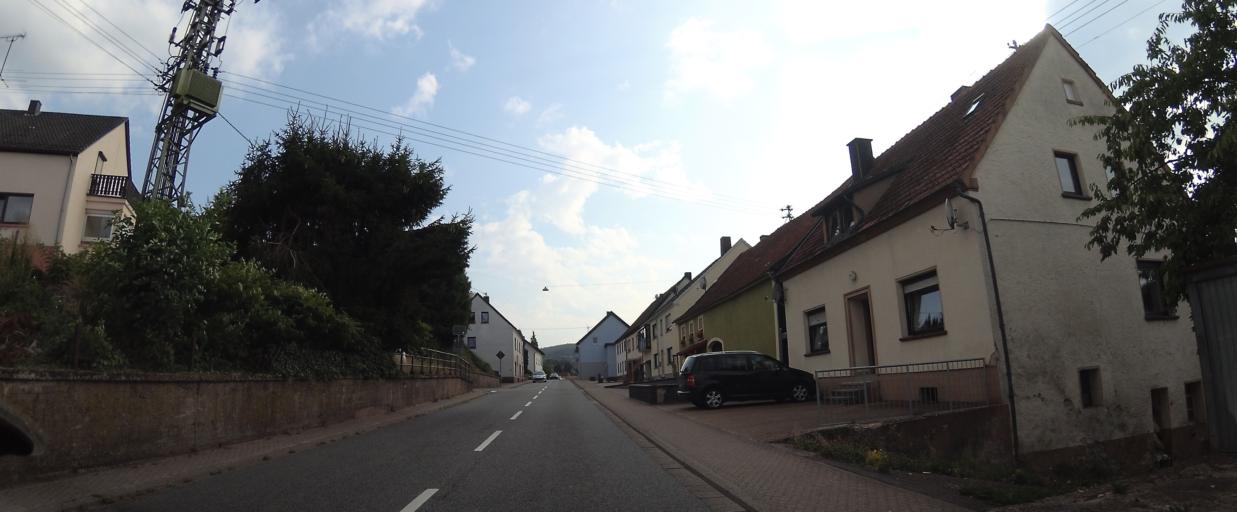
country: DE
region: Saarland
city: Tholey
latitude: 49.5337
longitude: 6.9756
